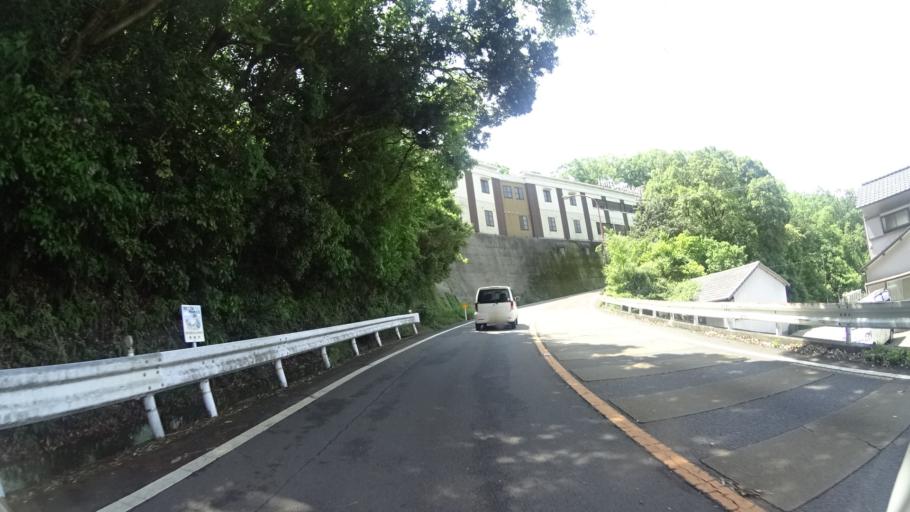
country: JP
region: Tokushima
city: Tokushima-shi
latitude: 34.0599
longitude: 134.5408
